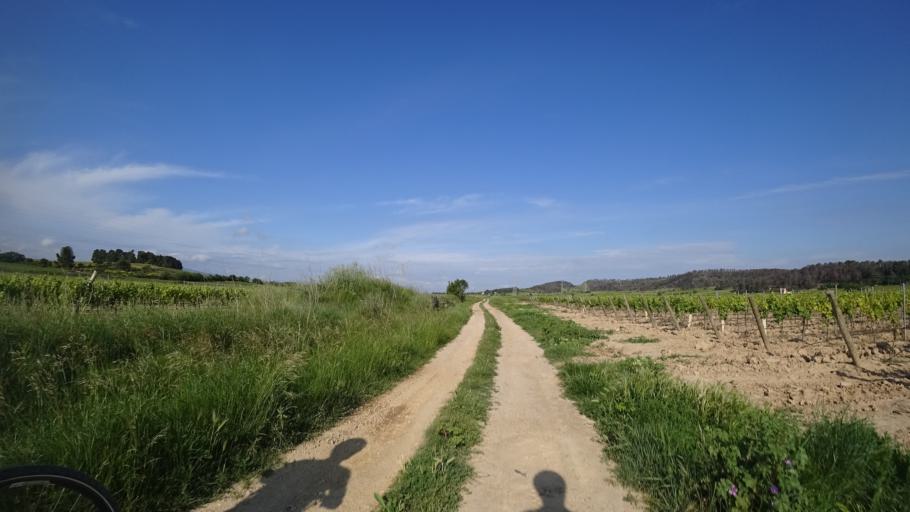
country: FR
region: Languedoc-Roussillon
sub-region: Departement de l'Herault
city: Olonzac
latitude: 43.2378
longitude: 2.7243
